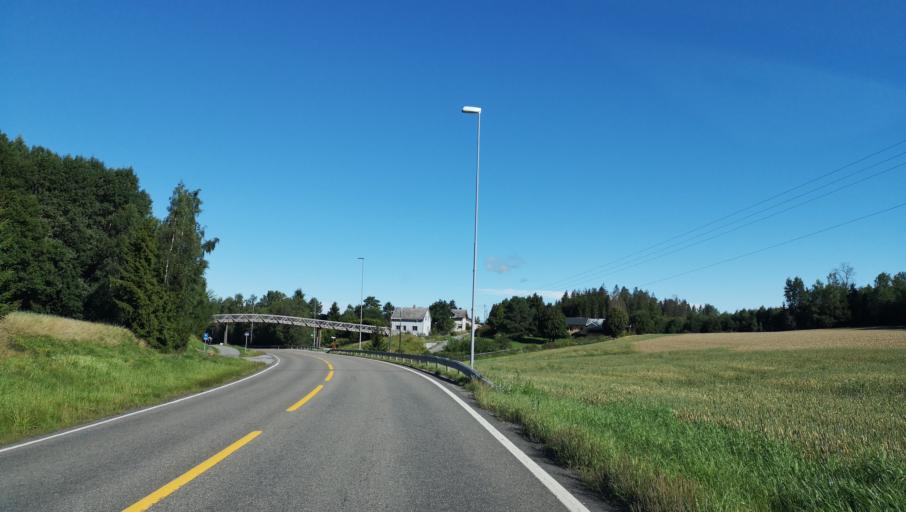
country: NO
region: Ostfold
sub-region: Spydeberg
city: Spydeberg
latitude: 59.5947
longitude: 11.1086
